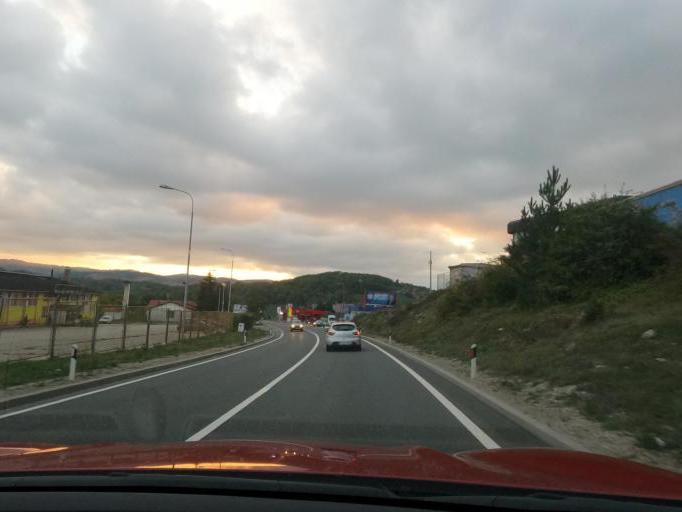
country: RS
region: Central Serbia
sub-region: Zlatiborski Okrug
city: Cajetina
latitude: 43.7923
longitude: 19.7616
